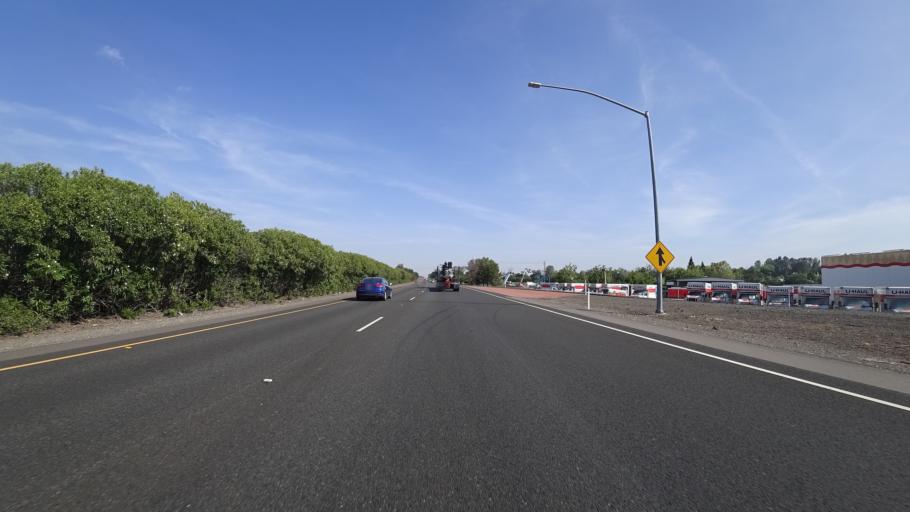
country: US
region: California
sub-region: Butte County
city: Chico
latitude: 39.7132
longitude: -121.7995
